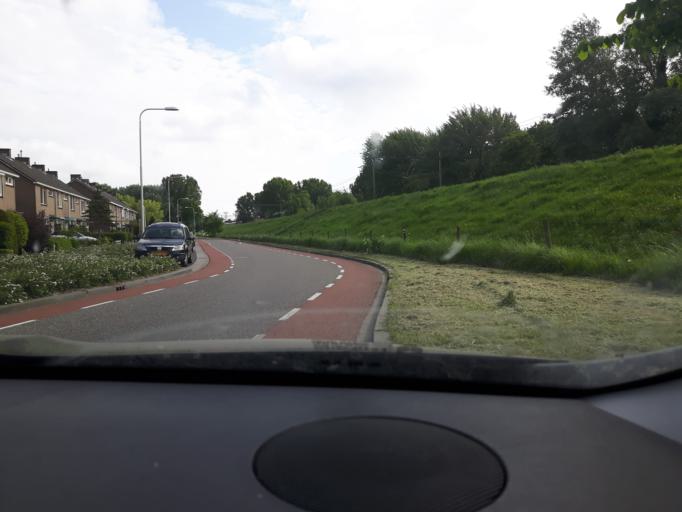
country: NL
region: Zeeland
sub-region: Gemeente Vlissingen
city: Vlissingen
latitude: 51.4604
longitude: 3.5938
